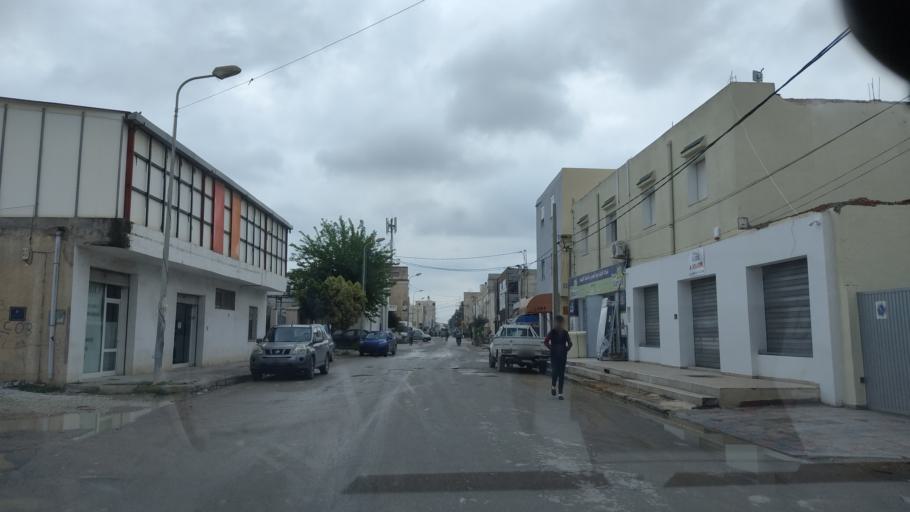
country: TN
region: Ariana
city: Ariana
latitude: 36.8755
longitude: 10.2182
